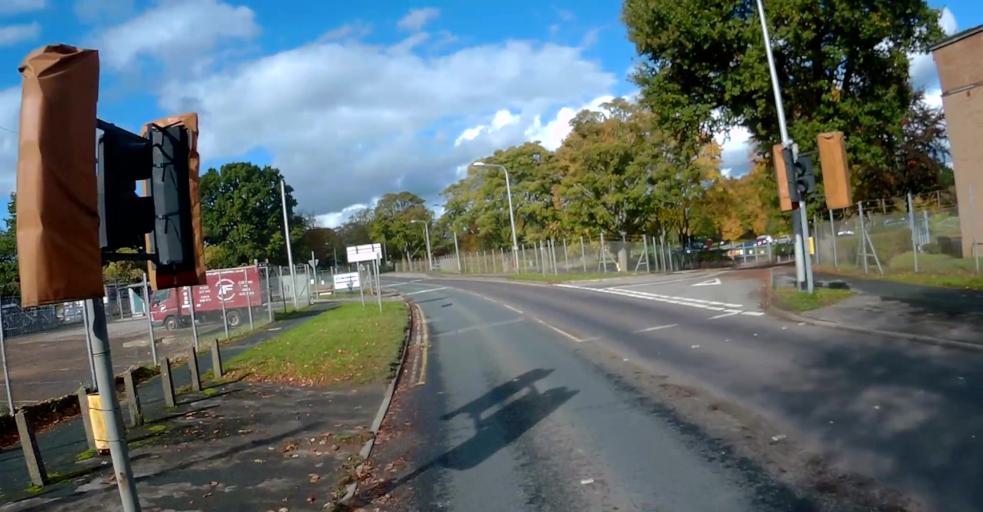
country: GB
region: England
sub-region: Hampshire
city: Aldershot
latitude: 51.2587
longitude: -0.7435
